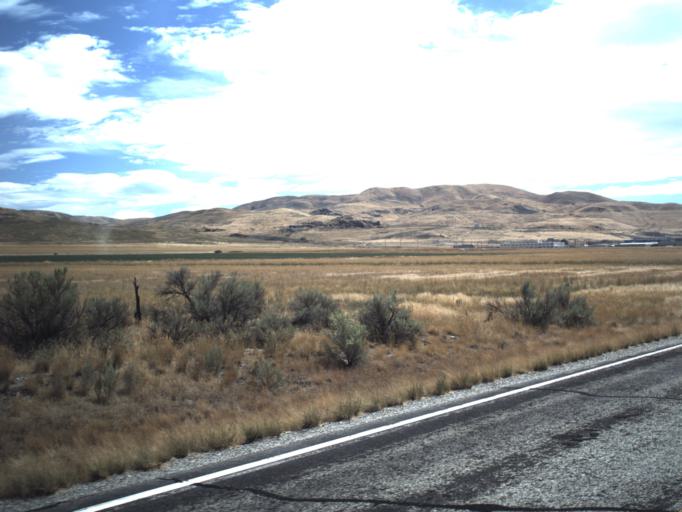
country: US
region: Utah
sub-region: Box Elder County
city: Tremonton
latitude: 41.7330
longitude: -112.4340
